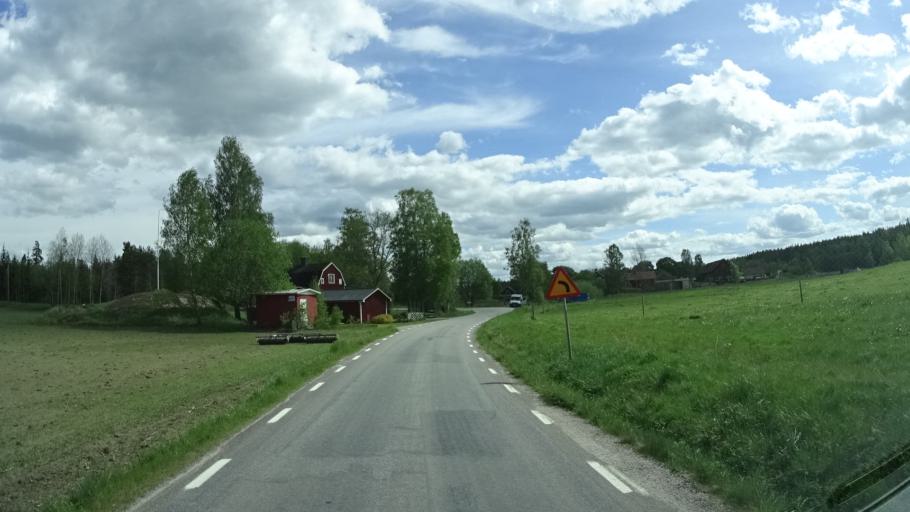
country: SE
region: OEstergoetland
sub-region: Finspangs Kommun
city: Finspang
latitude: 58.6094
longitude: 15.7049
